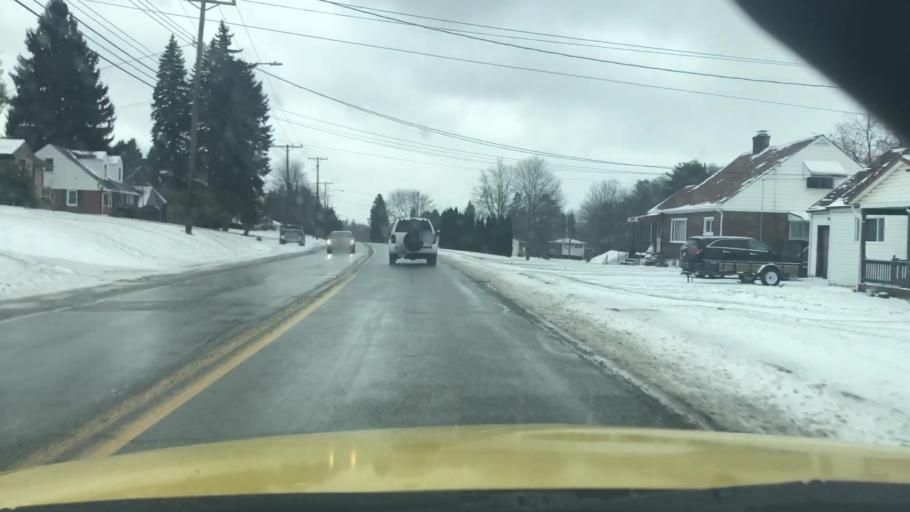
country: US
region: Pennsylvania
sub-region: Cambria County
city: Geistown
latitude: 40.2891
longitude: -78.8763
